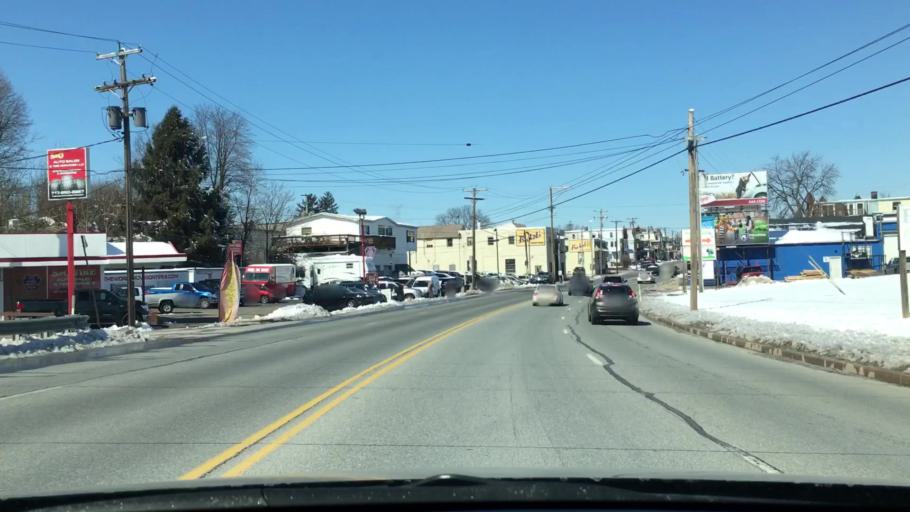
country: US
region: Pennsylvania
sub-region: York County
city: West York
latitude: 39.9502
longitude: -76.7468
